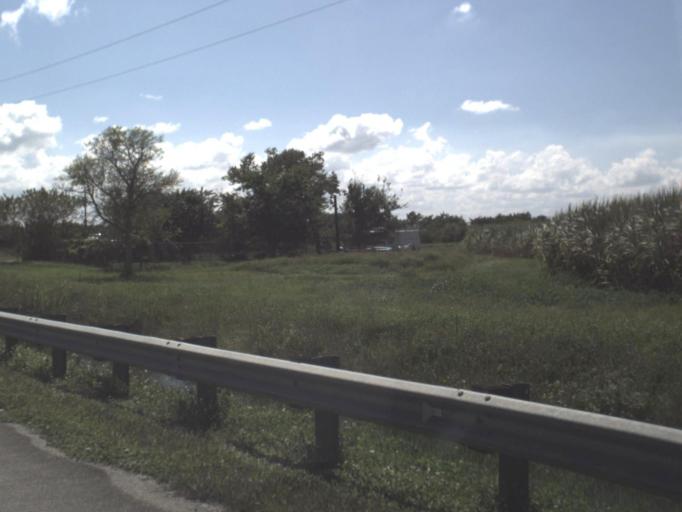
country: US
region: Florida
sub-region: Glades County
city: Moore Haven
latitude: 26.8537
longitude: -81.1228
